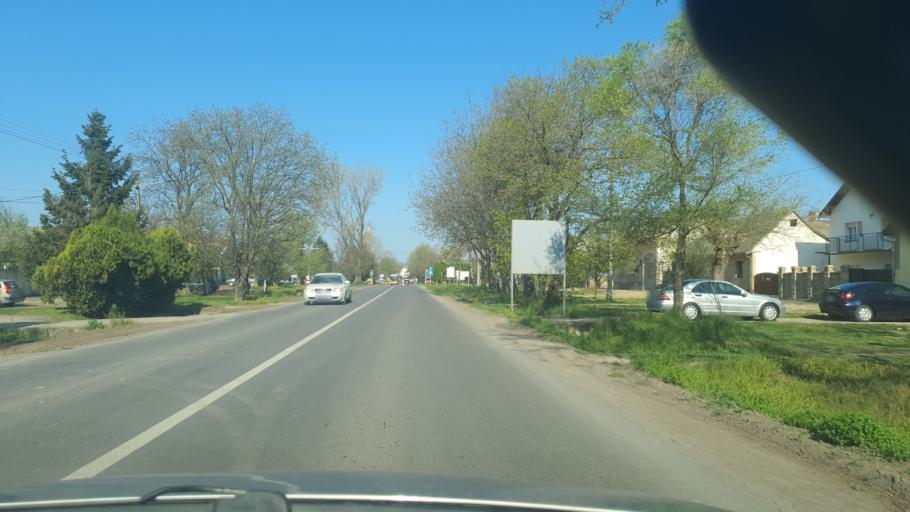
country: RS
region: Autonomna Pokrajina Vojvodina
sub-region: Zapadnobacki Okrug
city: Kula
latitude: 45.6076
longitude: 19.5420
